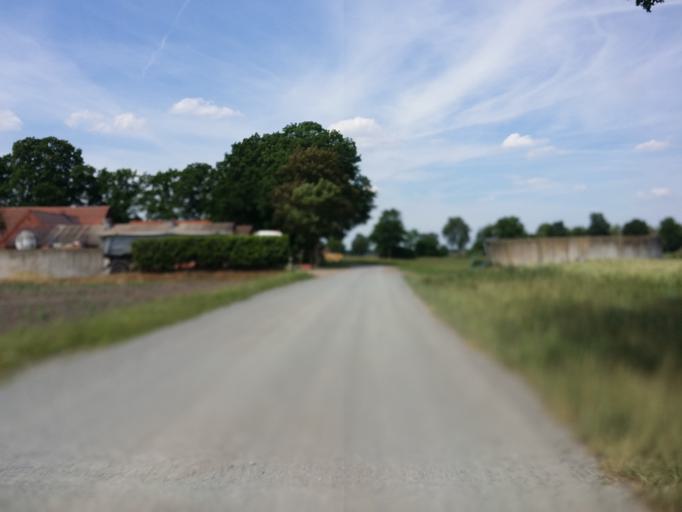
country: DE
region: Lower Saxony
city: Syke
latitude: 52.9663
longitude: 8.8677
